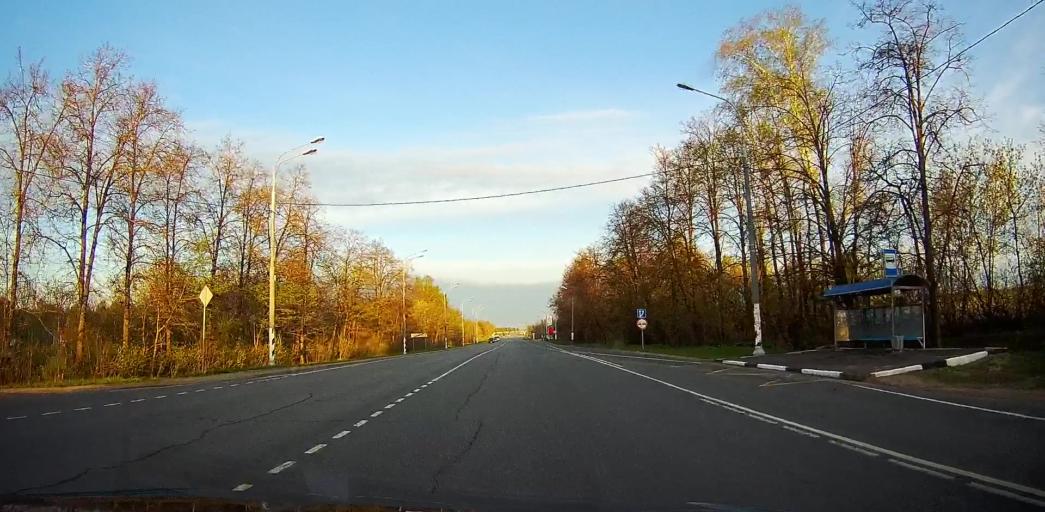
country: RU
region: Moskovskaya
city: Troitskoye
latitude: 55.2224
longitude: 38.5758
